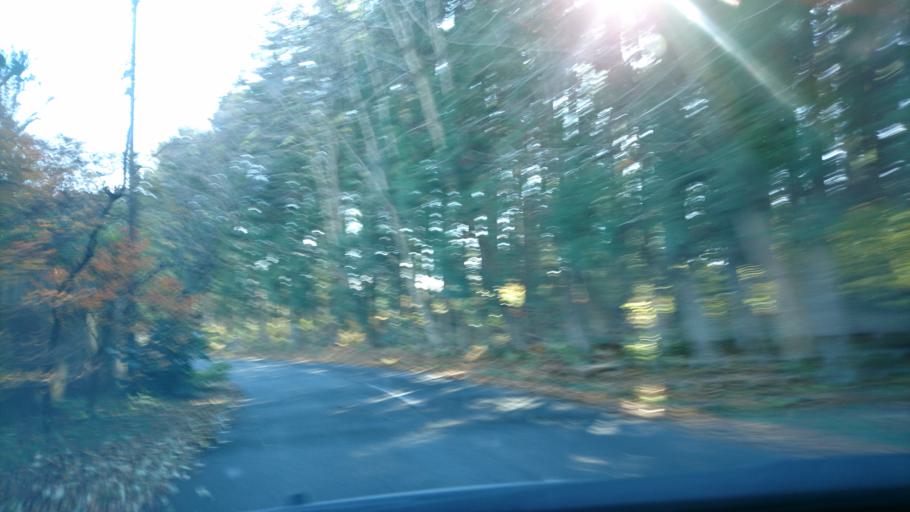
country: JP
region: Iwate
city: Ichinoseki
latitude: 38.9904
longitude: 141.1085
